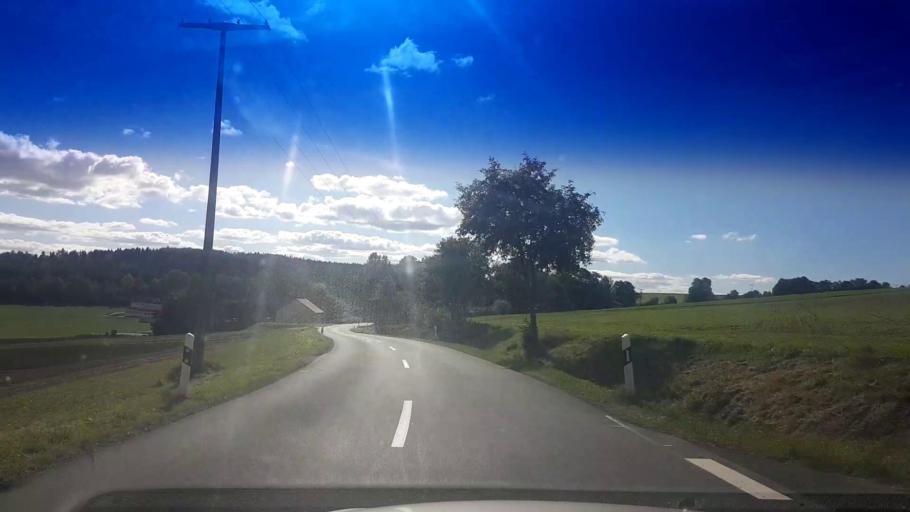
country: DE
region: Bavaria
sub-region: Upper Palatinate
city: Waldsassen
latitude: 50.0220
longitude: 12.2529
